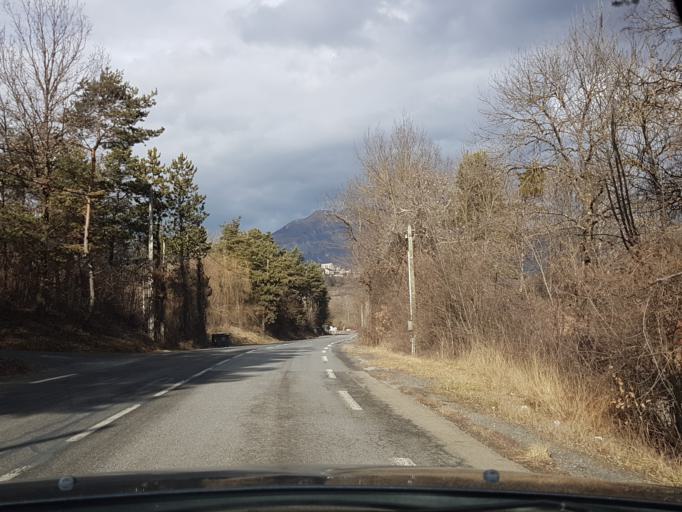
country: FR
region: Provence-Alpes-Cote d'Azur
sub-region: Departement des Hautes-Alpes
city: Gap
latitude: 44.5206
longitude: 6.0609
